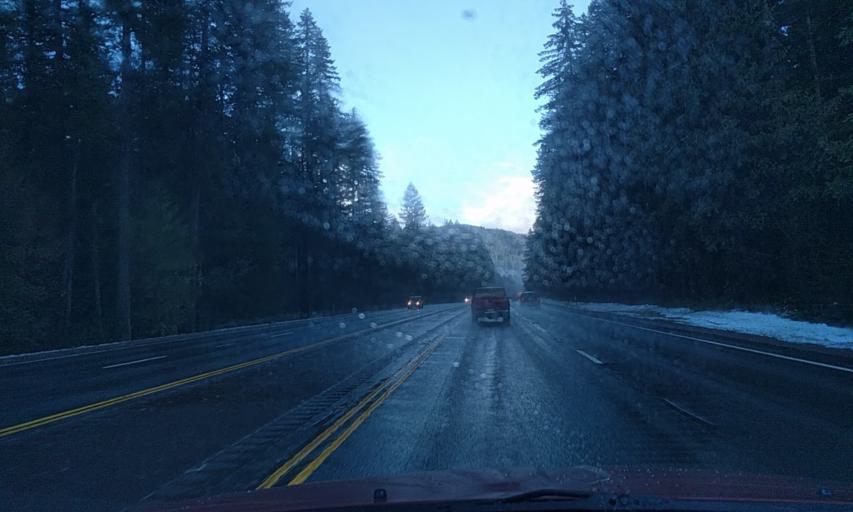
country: US
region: Oregon
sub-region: Clackamas County
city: Mount Hood Village
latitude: 45.3376
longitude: -121.9240
